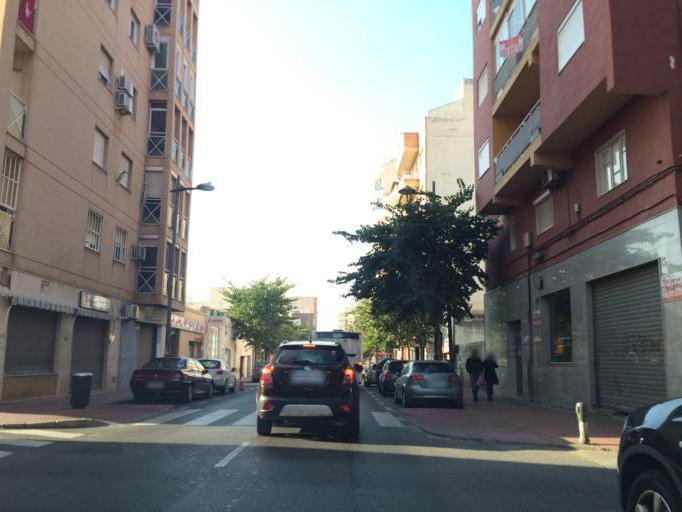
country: ES
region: Andalusia
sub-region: Provincia de Almeria
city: Almeria
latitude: 36.8470
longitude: -2.4582
